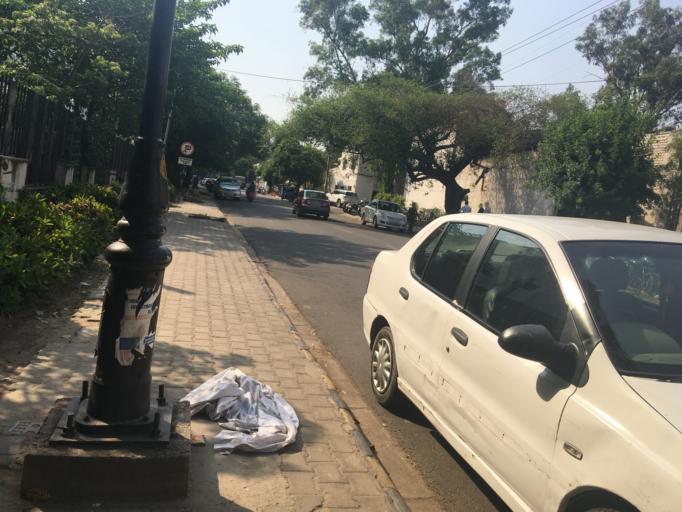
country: IN
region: Chandigarh
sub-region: Chandigarh
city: Chandigarh
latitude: 30.7054
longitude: 76.8024
